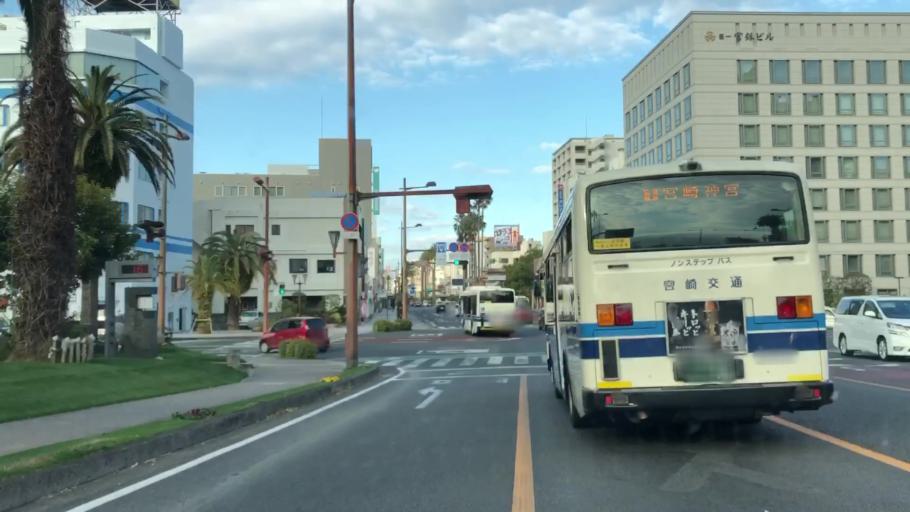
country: JP
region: Miyazaki
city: Miyazaki-shi
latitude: 31.9080
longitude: 131.4213
